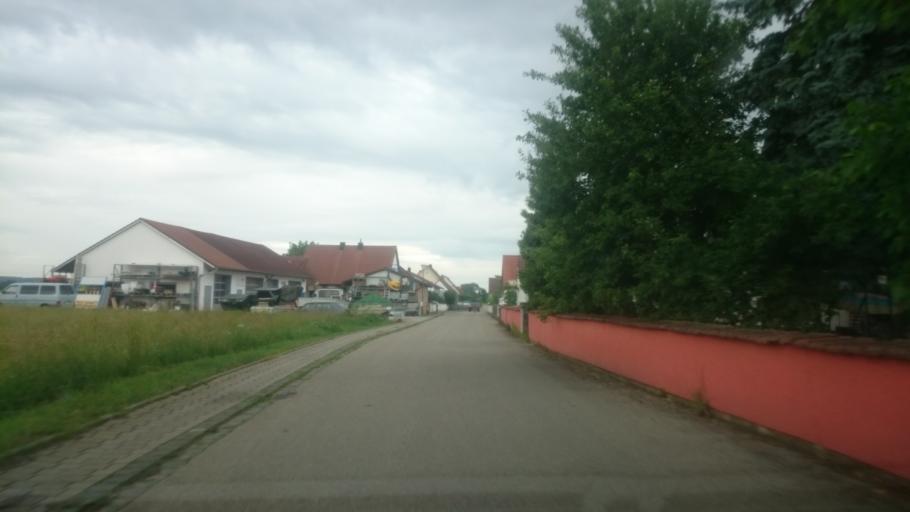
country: DE
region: Bavaria
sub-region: Upper Bavaria
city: Karlskron
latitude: 48.6919
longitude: 11.4228
